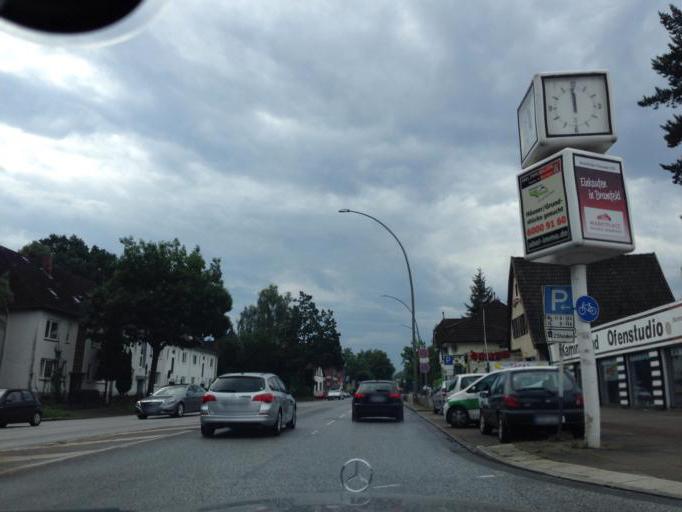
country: DE
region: Hamburg
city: Sasel
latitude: 53.6535
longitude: 10.1068
